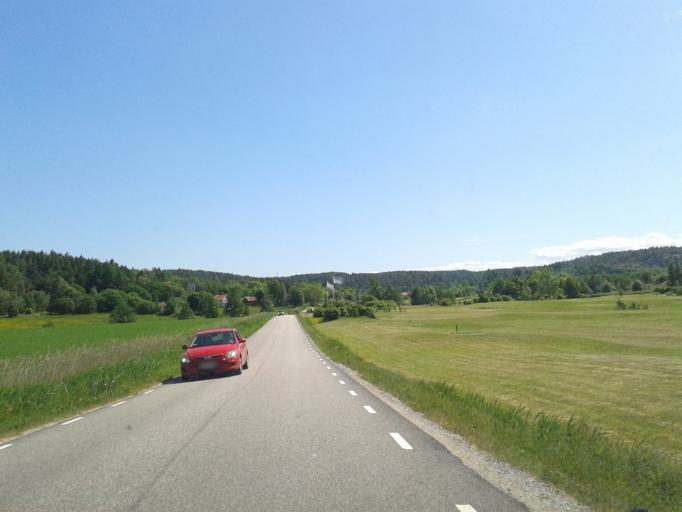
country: SE
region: Vaestra Goetaland
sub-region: Stenungsunds Kommun
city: Stora Hoga
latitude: 58.0284
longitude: 11.8708
